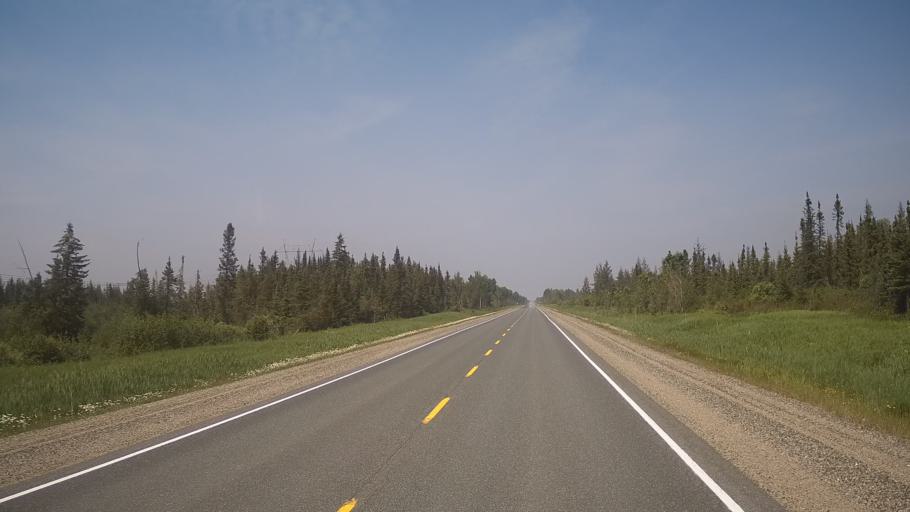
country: CA
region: Ontario
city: Timmins
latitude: 48.8027
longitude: -81.3677
